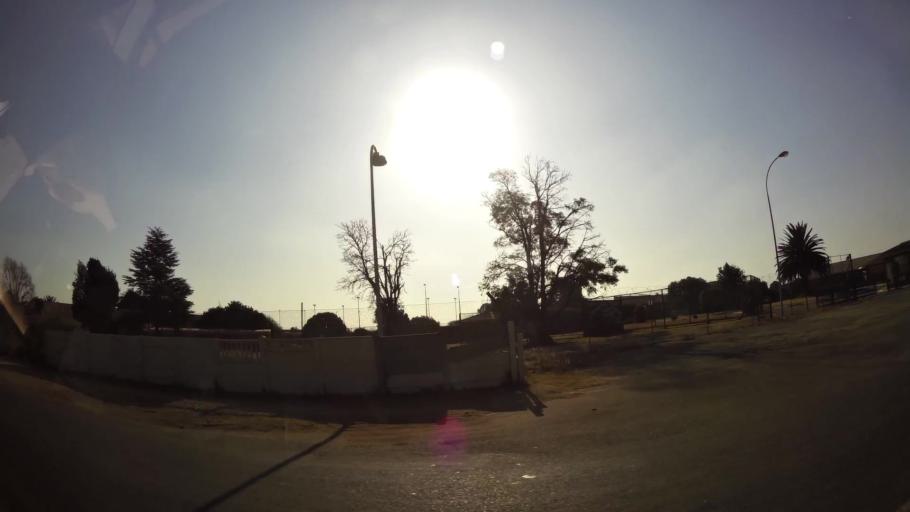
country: ZA
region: Gauteng
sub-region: West Rand District Municipality
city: Randfontein
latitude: -26.1568
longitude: 27.7155
